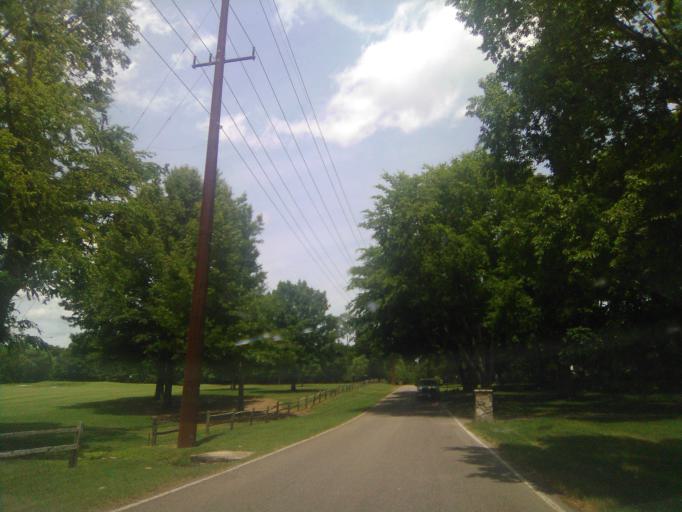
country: US
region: Tennessee
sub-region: Davidson County
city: Belle Meade
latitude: 36.0985
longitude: -86.8590
